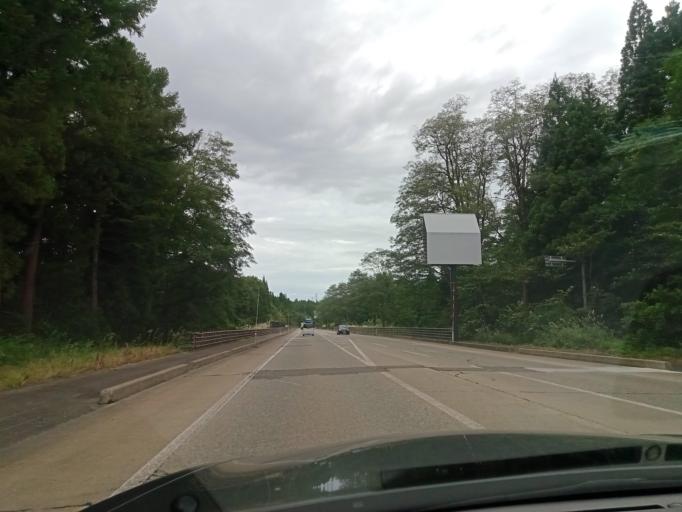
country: JP
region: Niigata
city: Arai
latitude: 36.8615
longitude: 138.1955
